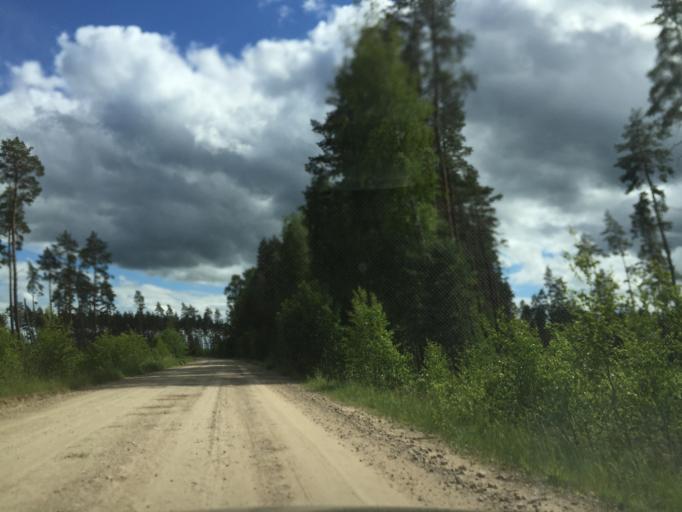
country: LV
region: Vecumnieki
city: Vecumnieki
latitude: 56.4889
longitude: 24.4079
